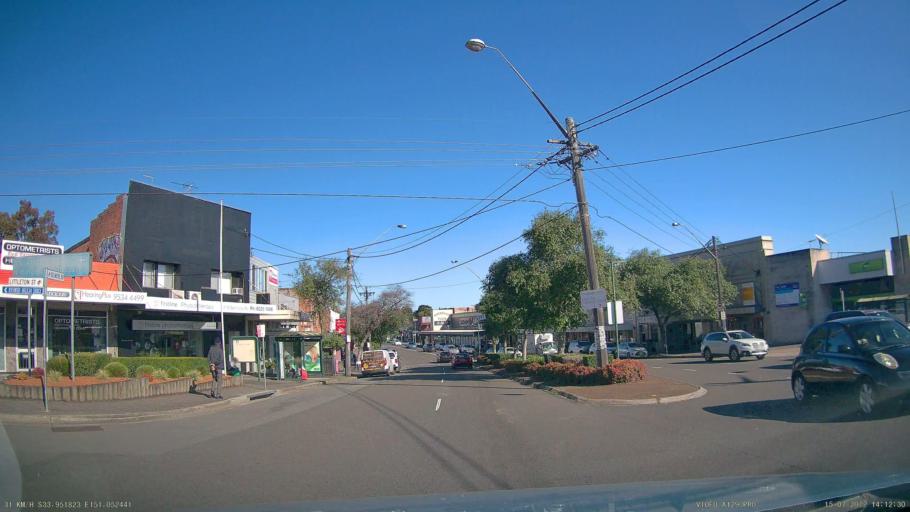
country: AU
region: New South Wales
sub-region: Hurstville
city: Peakhurst
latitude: -33.9519
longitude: 151.0524
